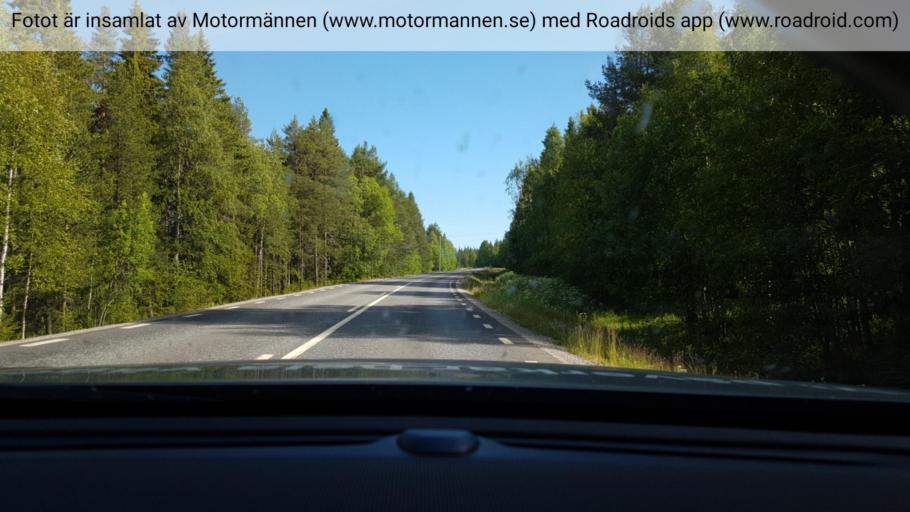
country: SE
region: Vaesterbotten
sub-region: Lycksele Kommun
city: Soderfors
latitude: 64.8157
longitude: 18.0719
